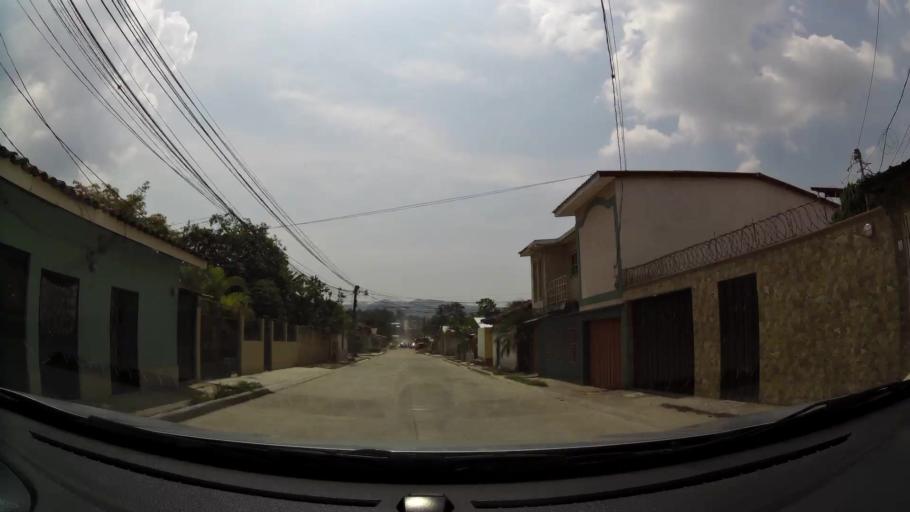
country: HN
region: Comayagua
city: Siguatepeque
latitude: 14.6034
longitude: -87.8305
